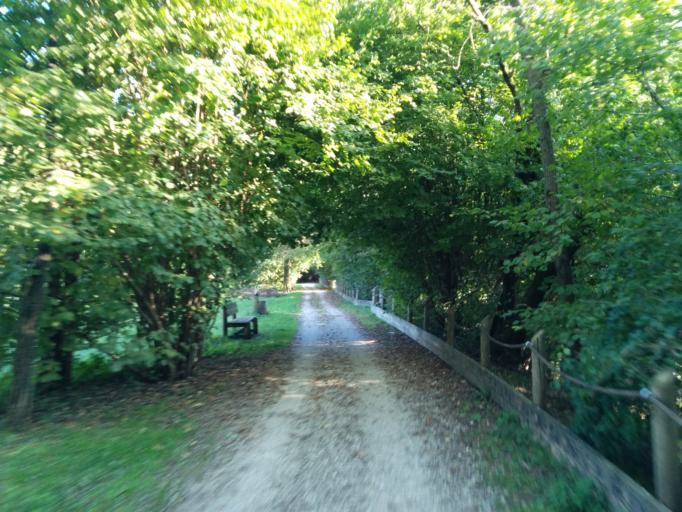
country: IT
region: Friuli Venezia Giulia
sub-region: Provincia di Udine
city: Reana del Roiale
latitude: 46.1247
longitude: 13.2066
